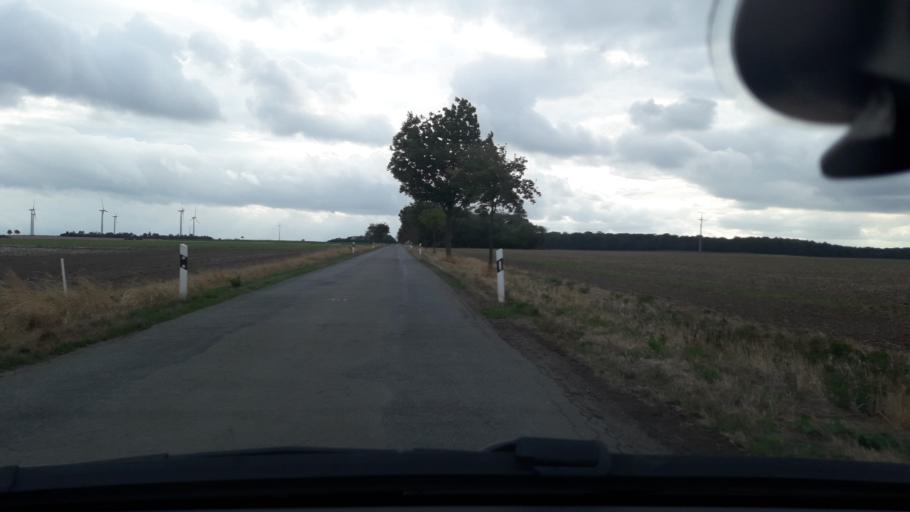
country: DE
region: Lower Saxony
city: Velpke
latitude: 52.3911
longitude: 10.9623
